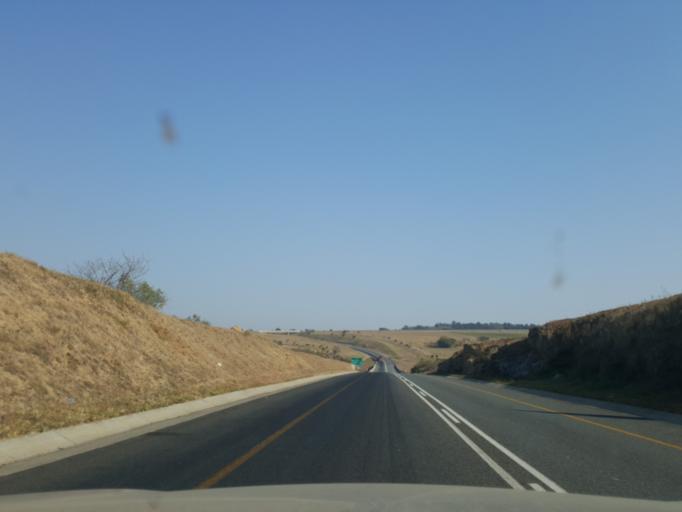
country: ZA
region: Mpumalanga
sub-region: Ehlanzeni District
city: Nelspruit
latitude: -25.4478
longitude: 31.0052
